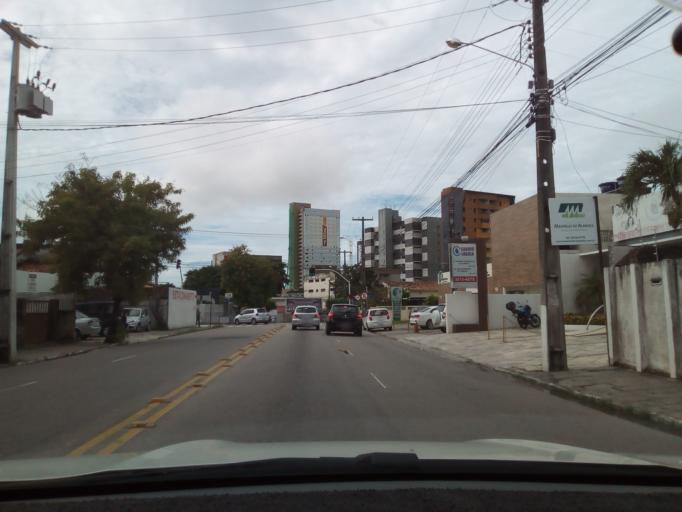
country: BR
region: Paraiba
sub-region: Joao Pessoa
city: Joao Pessoa
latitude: -7.1222
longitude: -34.8585
